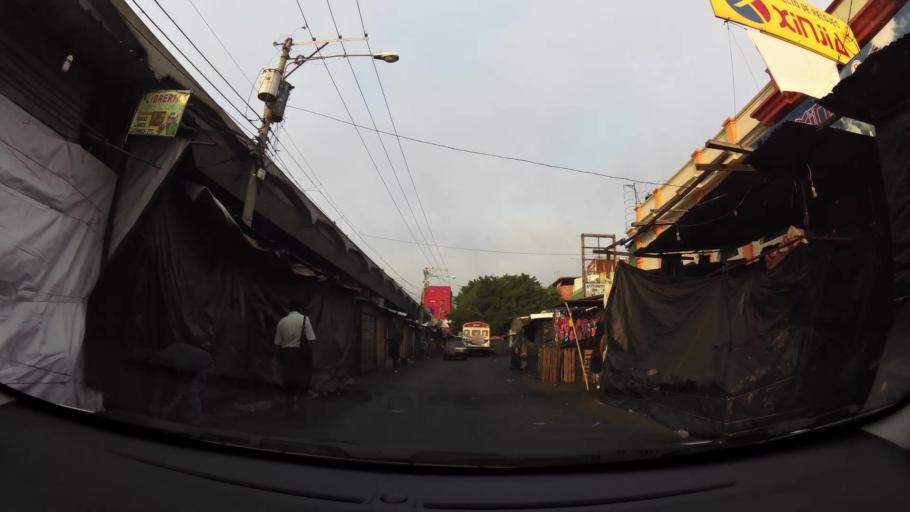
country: SV
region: San Salvador
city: San Salvador
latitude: 13.6973
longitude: -89.1927
